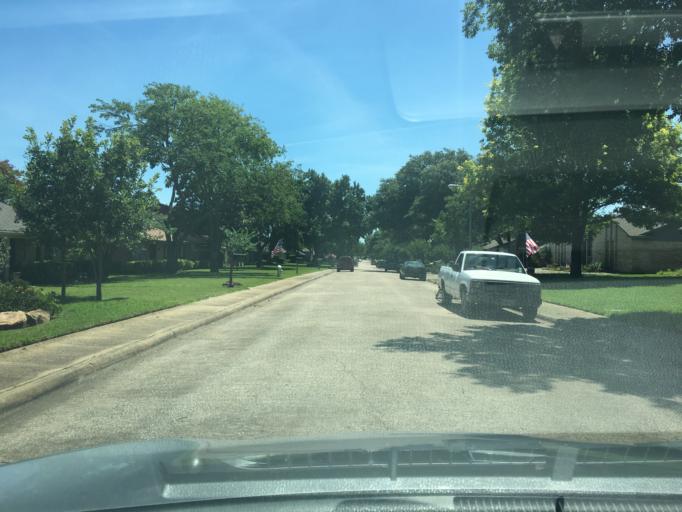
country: US
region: Texas
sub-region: Dallas County
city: Richardson
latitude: 32.9468
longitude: -96.6940
